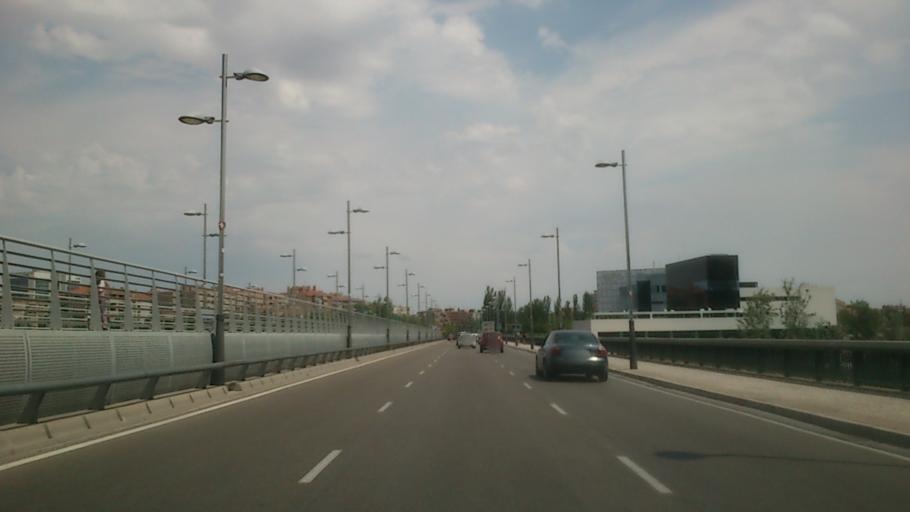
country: ES
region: Aragon
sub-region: Provincia de Zaragoza
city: Almozara
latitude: 41.6603
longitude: -0.8911
